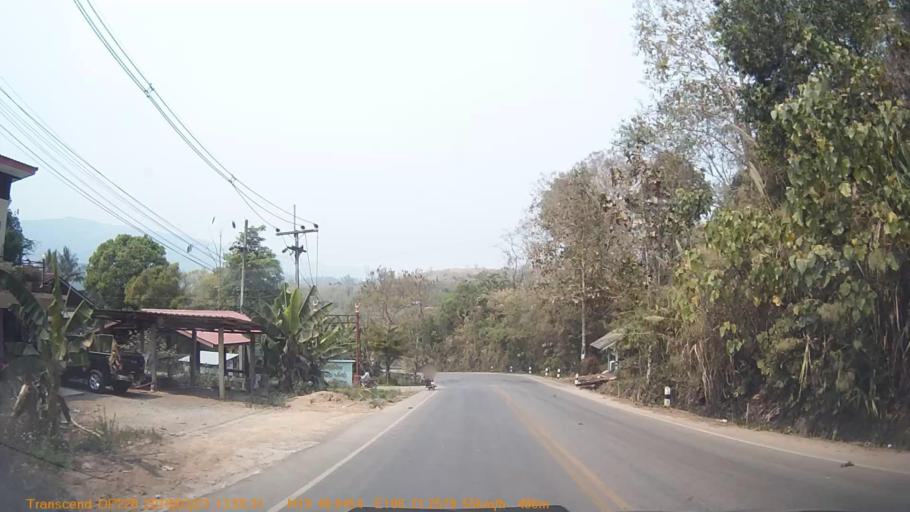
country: TH
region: Chiang Rai
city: Khun Tan
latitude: 19.8010
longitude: 100.3543
